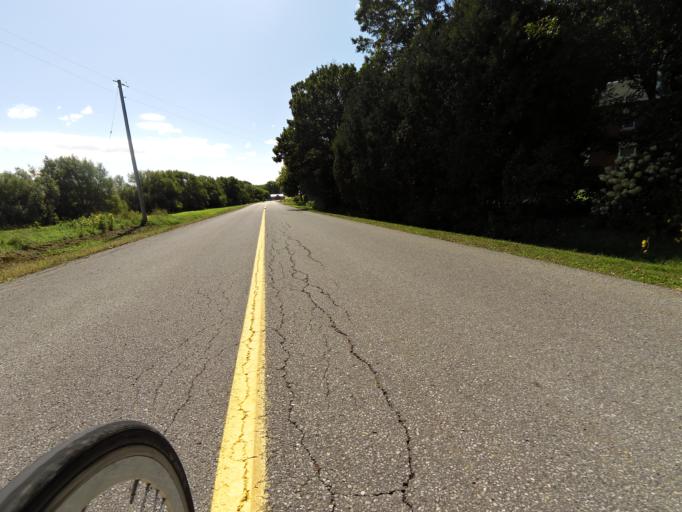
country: CA
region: Ontario
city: Bells Corners
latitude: 45.2373
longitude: -75.8086
